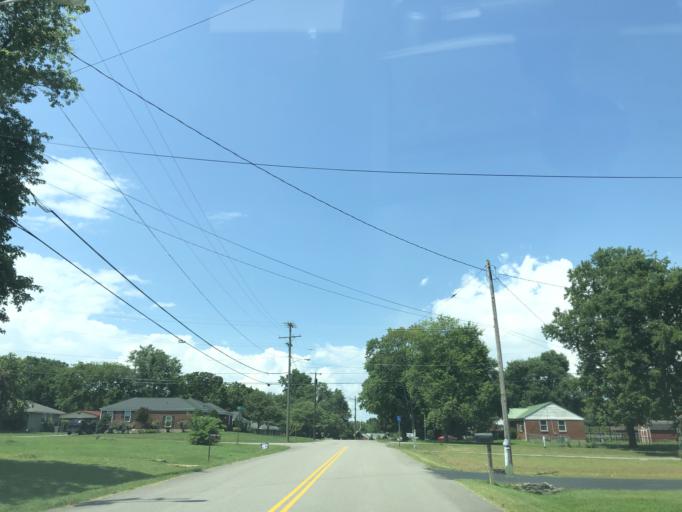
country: US
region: Tennessee
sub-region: Davidson County
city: Lakewood
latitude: 36.1563
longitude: -86.6616
